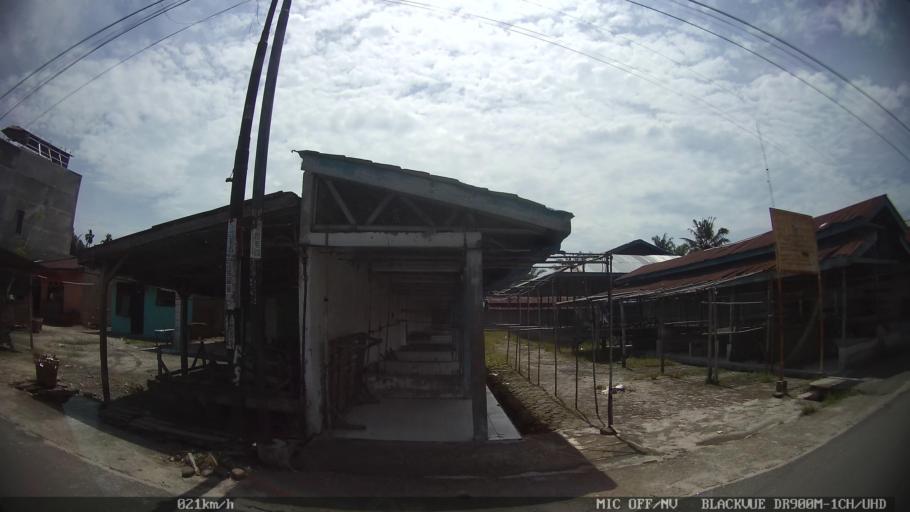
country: ID
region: North Sumatra
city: Percut
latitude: 3.5980
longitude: 98.8602
